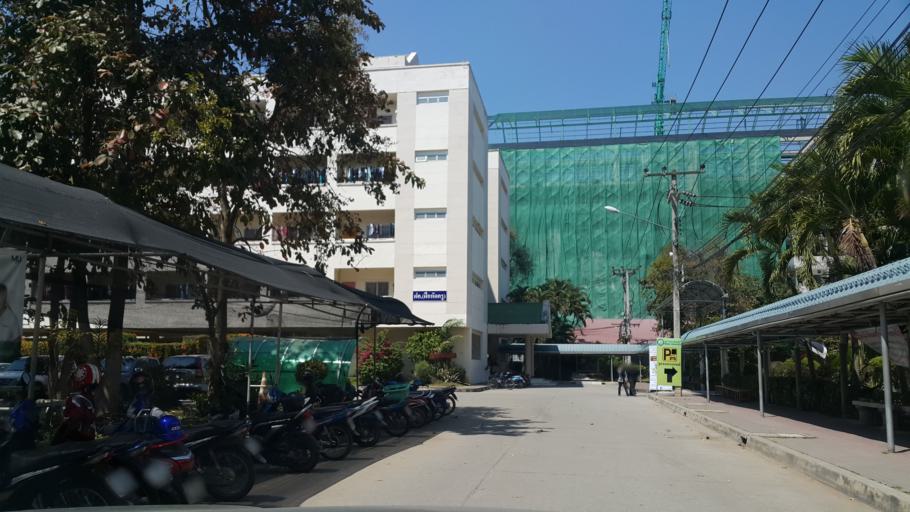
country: TH
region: Chiang Mai
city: San Sai
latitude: 18.8993
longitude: 99.0090
